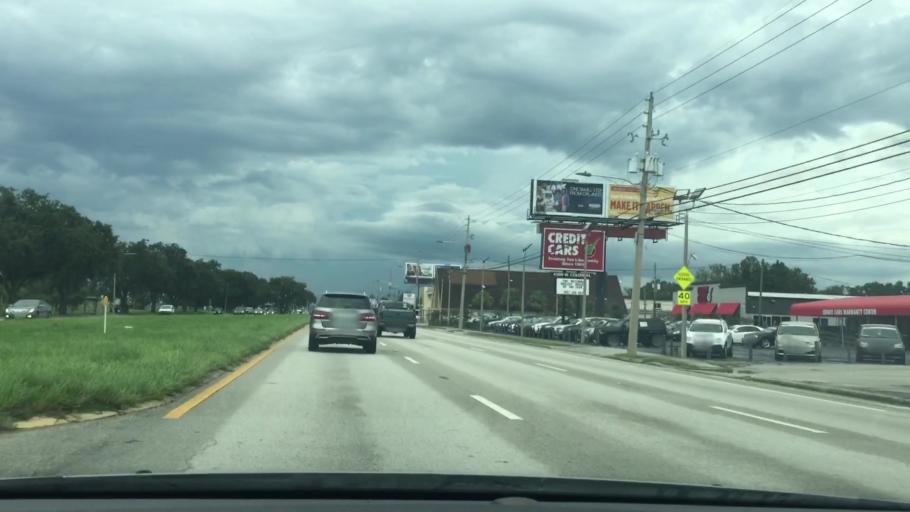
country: US
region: Florida
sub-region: Orange County
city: Pine Hills
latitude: 28.5525
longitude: -81.4370
